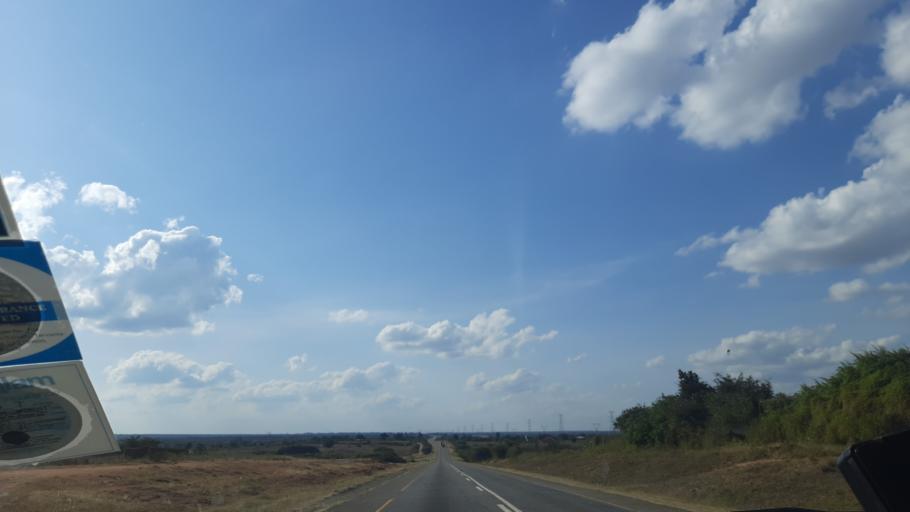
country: TZ
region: Singida
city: Ikungi
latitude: -5.1998
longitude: 34.7841
